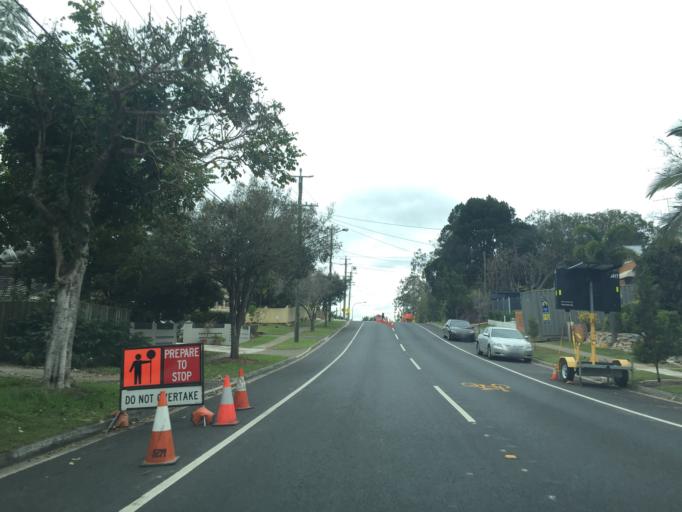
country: AU
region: Queensland
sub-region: Brisbane
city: Everton Park
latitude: -27.4385
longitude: 152.9860
